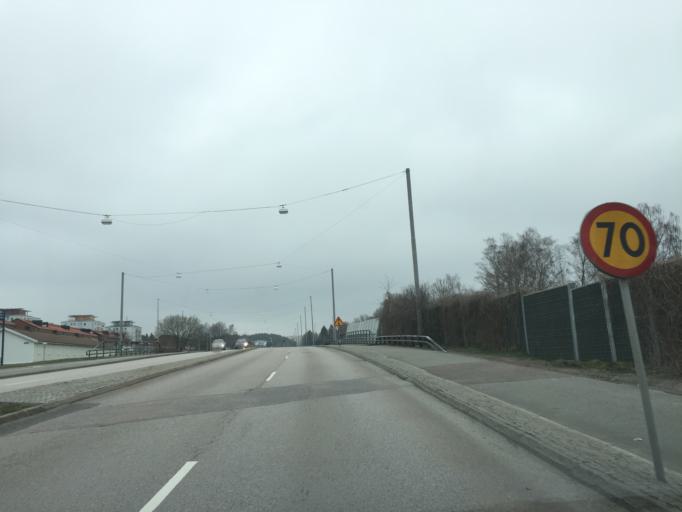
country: SE
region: Vaestra Goetaland
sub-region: Goteborg
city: Eriksbo
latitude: 57.7462
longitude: 12.0345
